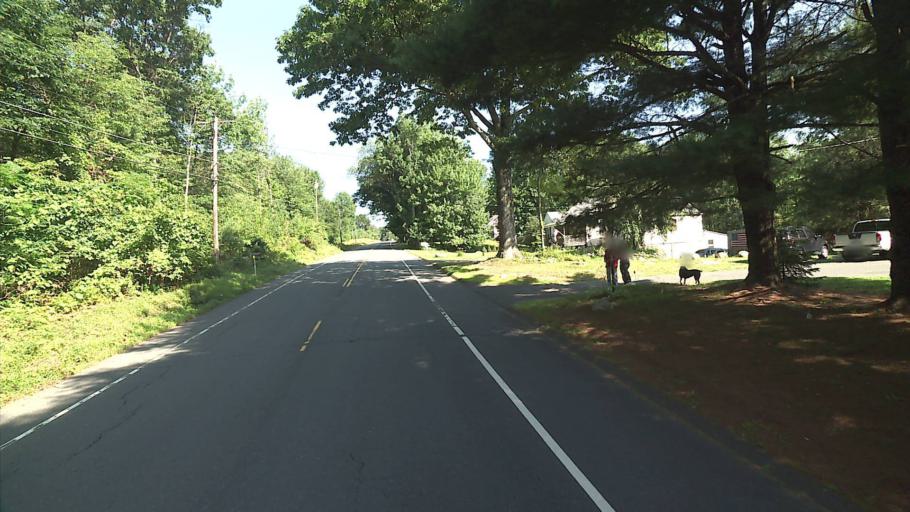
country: US
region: Connecticut
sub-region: Hartford County
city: North Granby
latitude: 41.9914
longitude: -72.8976
